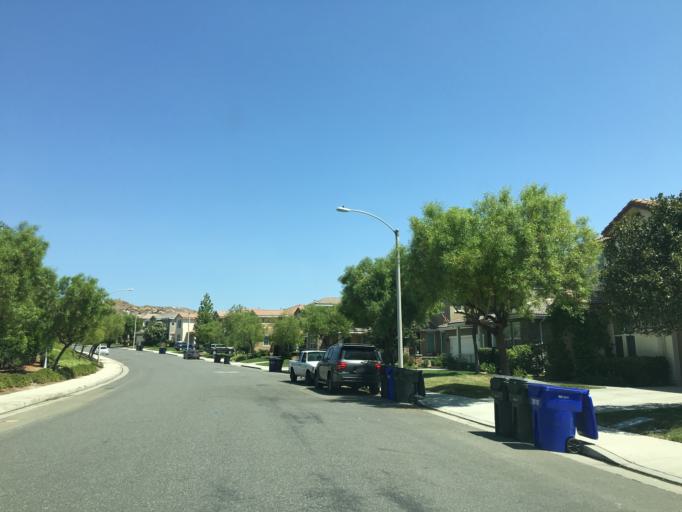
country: US
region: California
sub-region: Los Angeles County
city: Valencia
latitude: 34.4692
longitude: -118.5542
